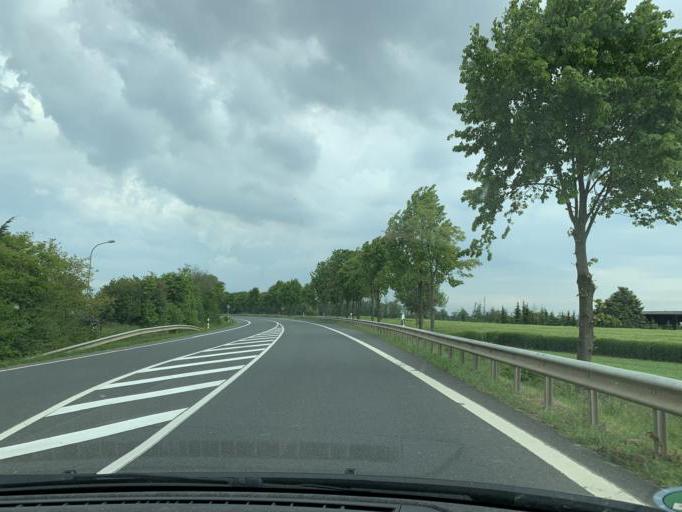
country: DE
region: North Rhine-Westphalia
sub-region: Regierungsbezirk Koln
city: Norvenich
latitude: 50.7591
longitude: 6.6351
